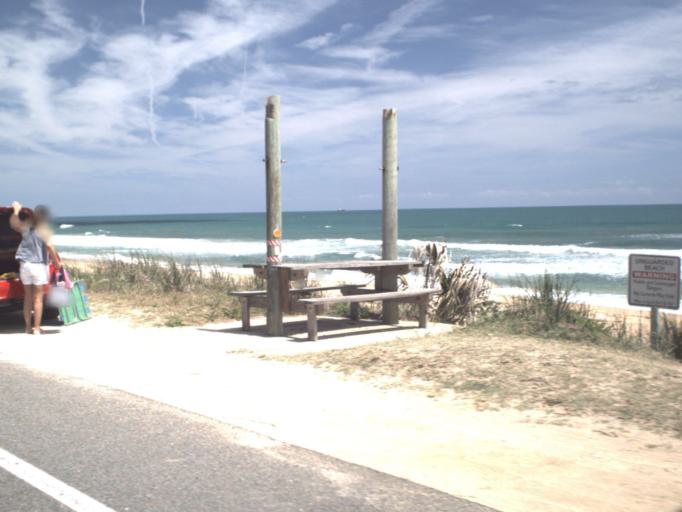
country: US
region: Florida
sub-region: Flagler County
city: Flagler Beach
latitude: 29.4894
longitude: -81.1315
